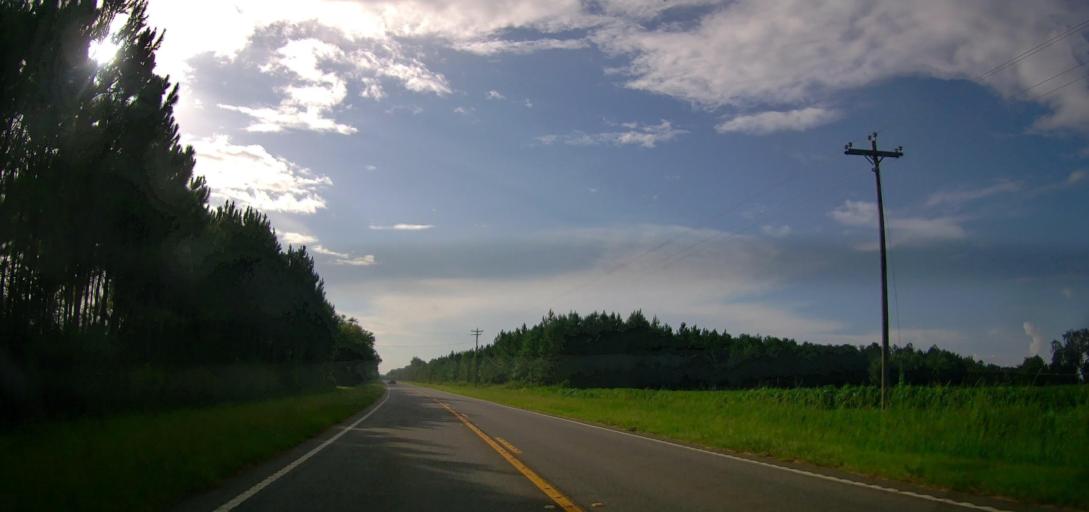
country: US
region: Georgia
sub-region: Coffee County
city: Nicholls
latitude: 31.3320
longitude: -82.5881
